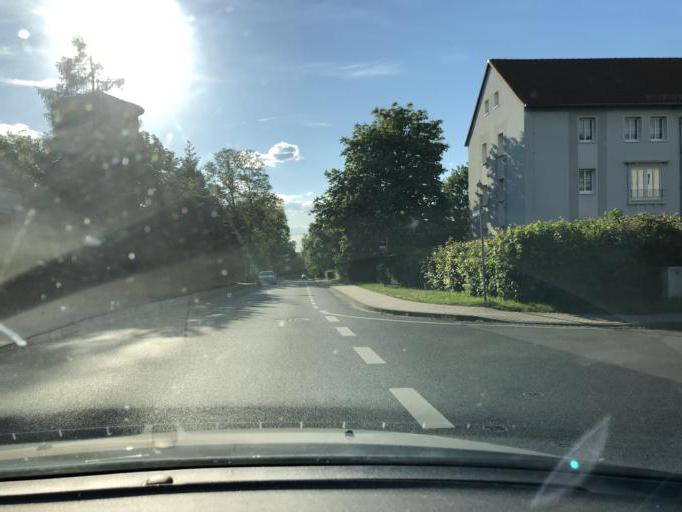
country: DE
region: Thuringia
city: Meuselwitz
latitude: 51.0388
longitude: 12.3116
